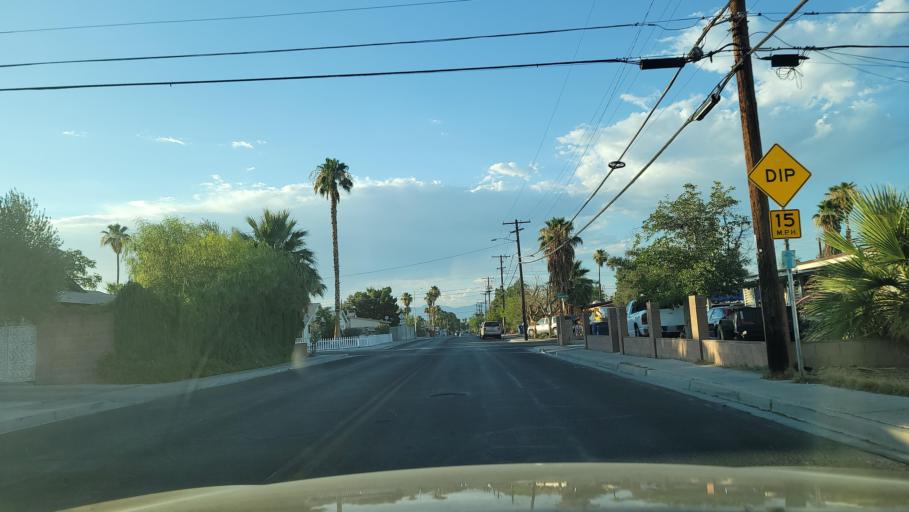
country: US
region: Nevada
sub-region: Clark County
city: Winchester
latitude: 36.1526
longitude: -115.1233
